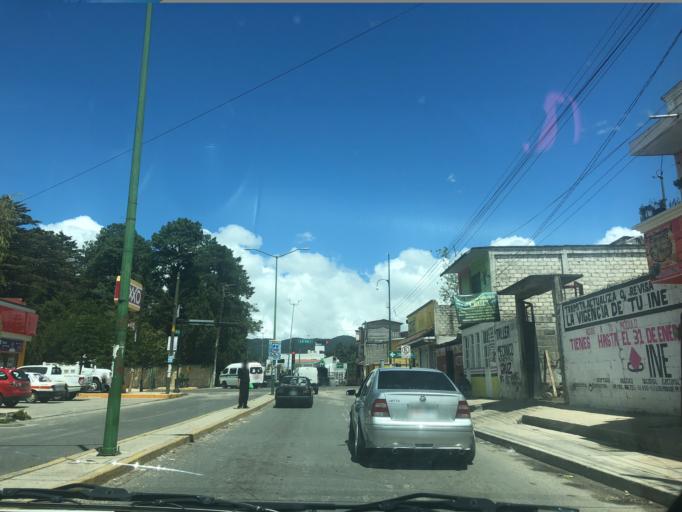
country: MX
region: Chiapas
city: San Cristobal de las Casas
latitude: 16.7205
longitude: -92.6400
